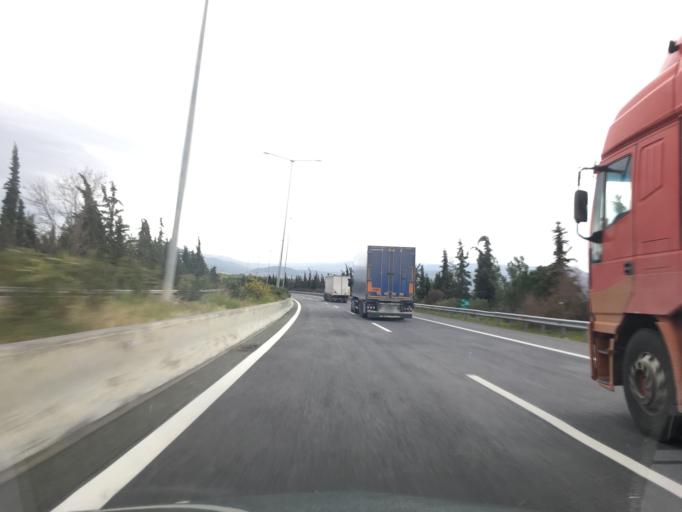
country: GR
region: Thessaly
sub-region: Nomos Magnisias
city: Evxinoupolis
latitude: 39.2389
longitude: 22.7337
